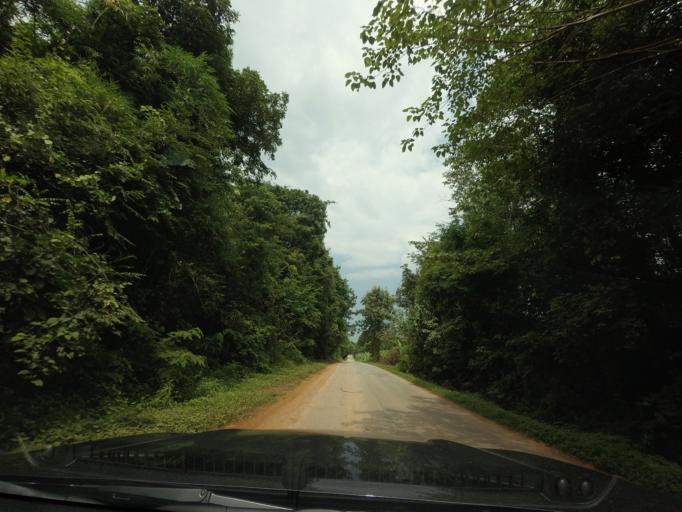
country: TH
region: Uttaradit
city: Fak Tha
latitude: 17.7795
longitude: 100.9218
